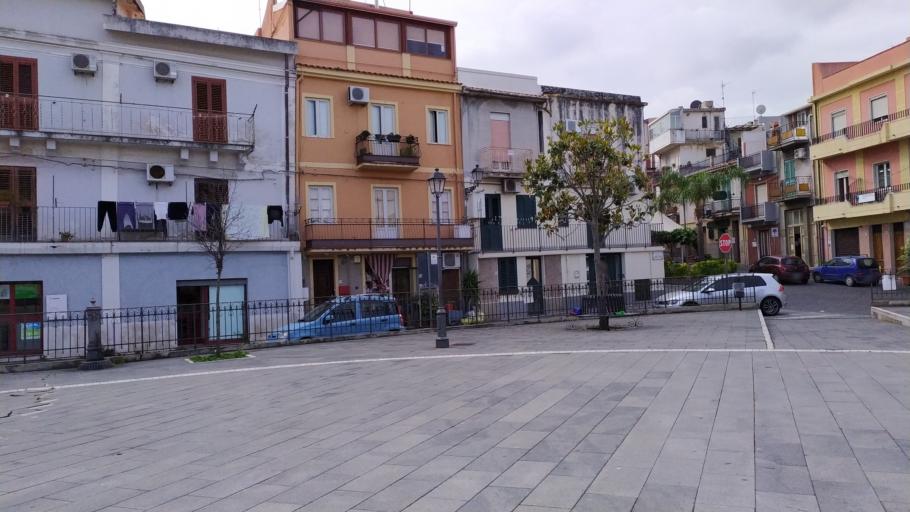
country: IT
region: Sicily
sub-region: Messina
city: San Pier Niceto
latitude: 38.1602
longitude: 15.3493
